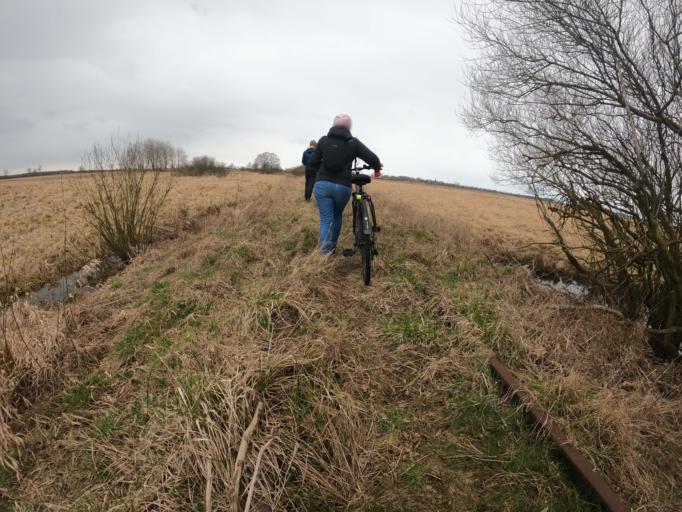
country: PL
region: West Pomeranian Voivodeship
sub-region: Powiat gryficki
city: Trzebiatow
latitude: 54.0757
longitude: 15.2359
